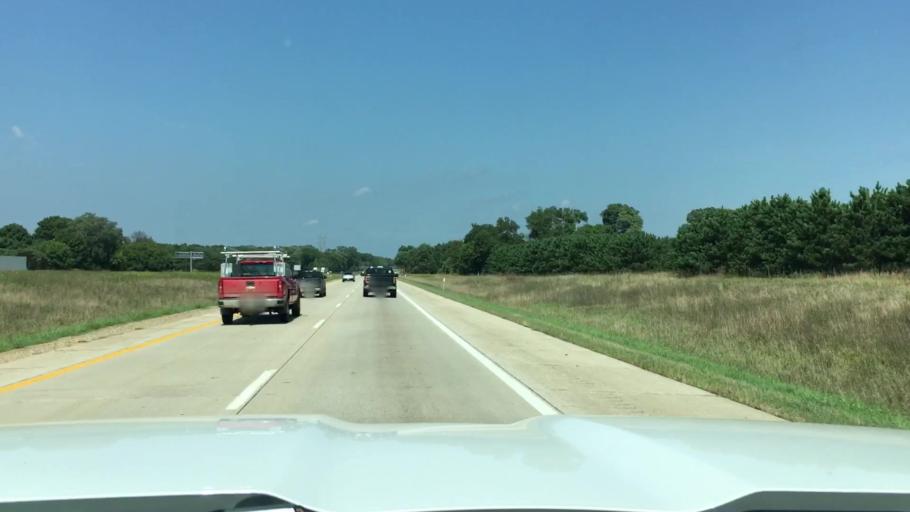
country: US
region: Michigan
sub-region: Allegan County
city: Plainwell
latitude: 42.3955
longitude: -85.6586
